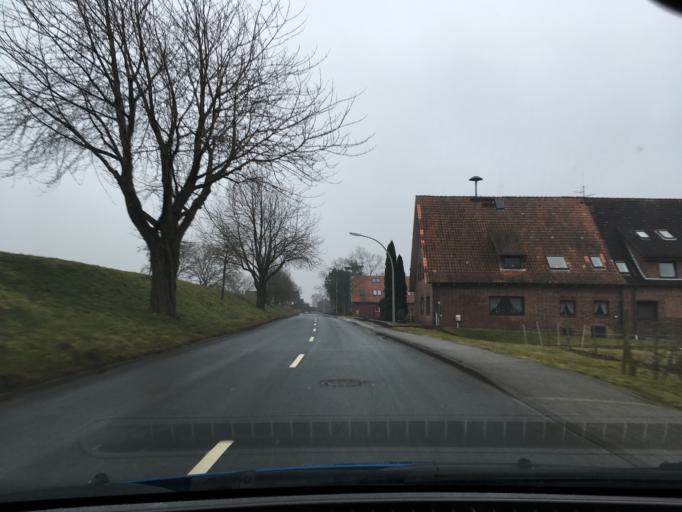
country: DE
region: Lower Saxony
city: Neu Wulmstorf
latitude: 53.5075
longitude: 9.8402
